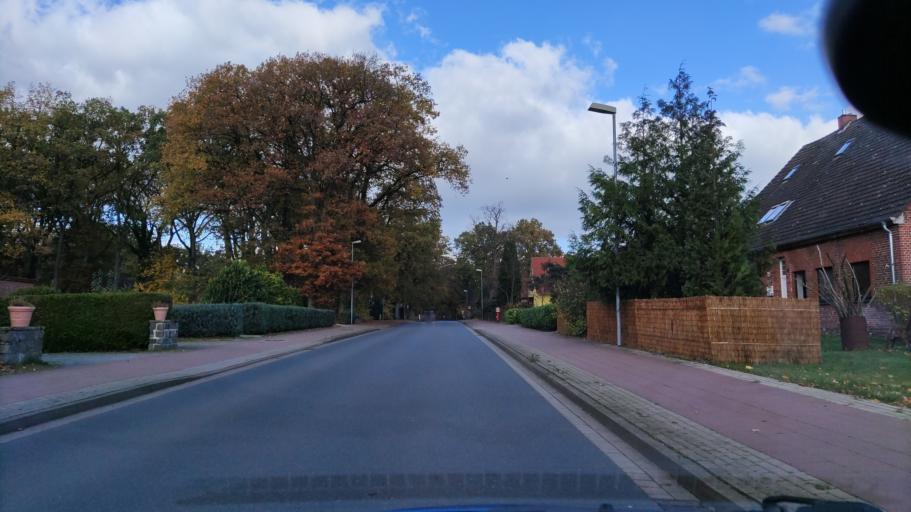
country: DE
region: Lower Saxony
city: Munster
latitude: 53.0134
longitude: 10.0870
